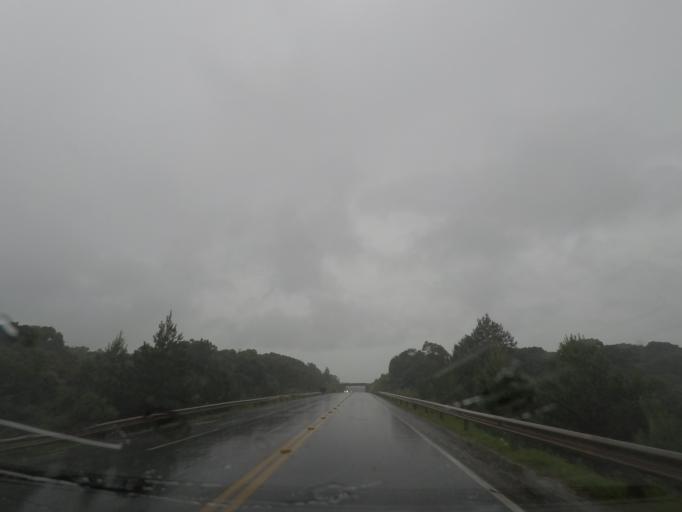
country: BR
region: Parana
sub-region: Almirante Tamandare
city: Almirante Tamandare
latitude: -25.3607
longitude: -49.3141
